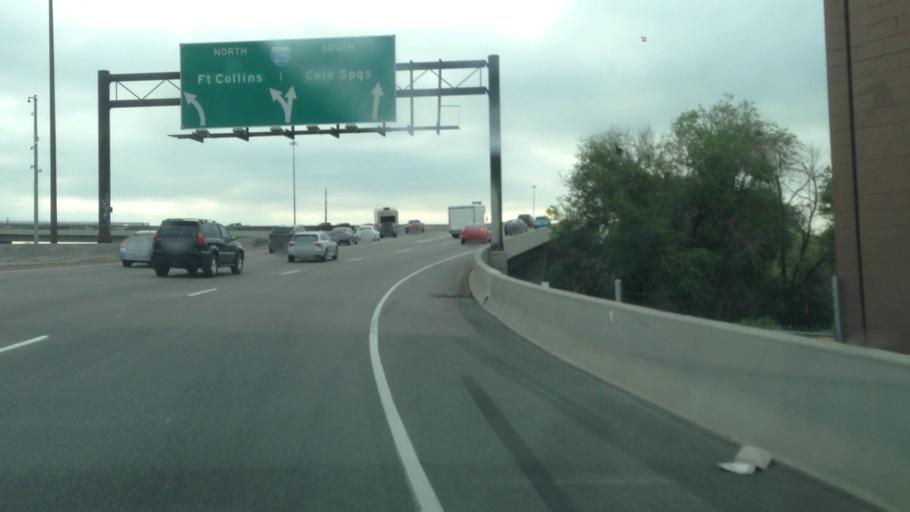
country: US
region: Colorado
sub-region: Denver County
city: Denver
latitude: 39.7250
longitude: -105.0163
